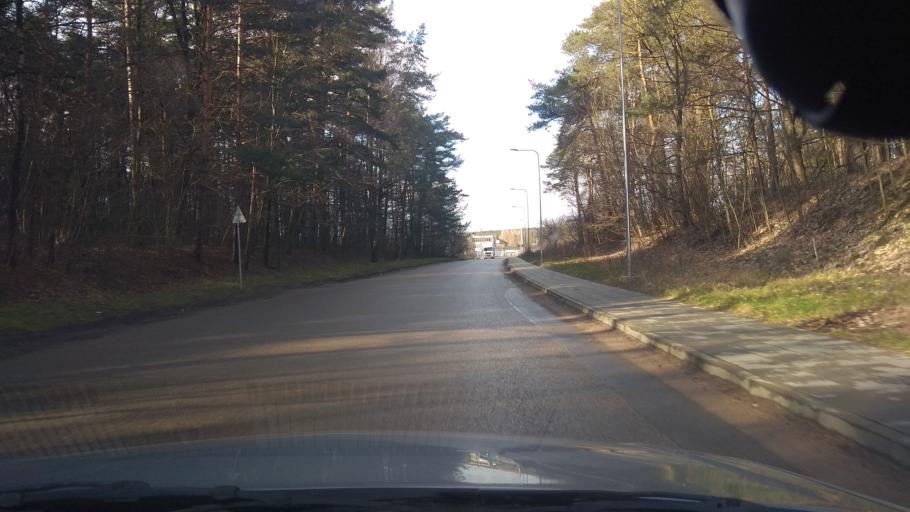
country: LT
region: Vilnius County
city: Lazdynai
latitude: 54.6446
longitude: 25.2212
